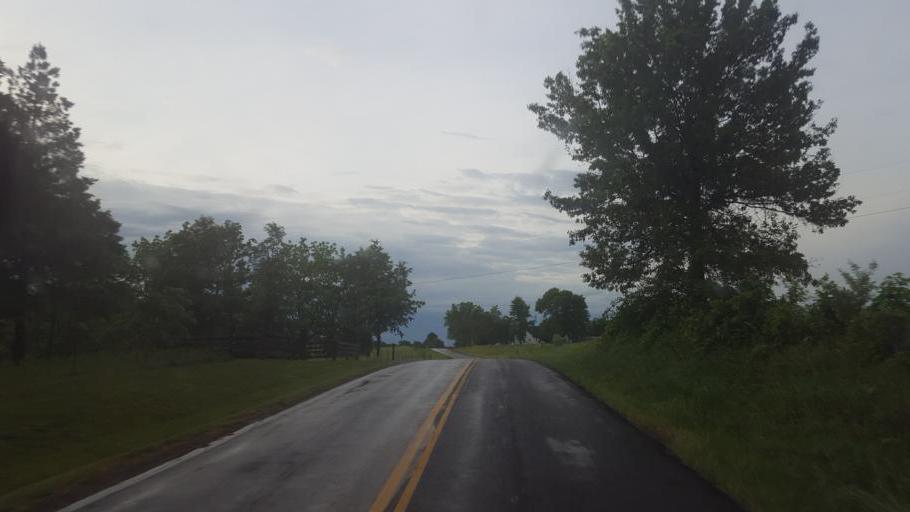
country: US
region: Missouri
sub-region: Moniteau County
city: California
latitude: 38.6648
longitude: -92.5831
